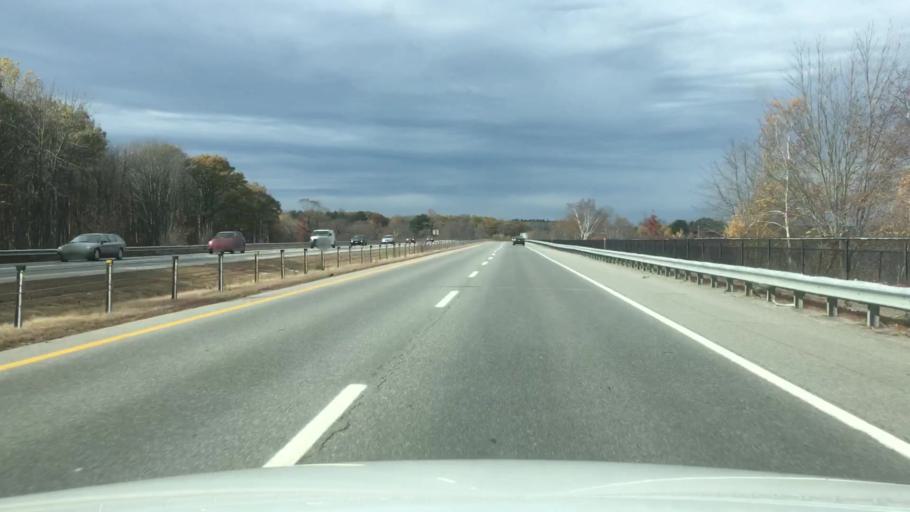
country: US
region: Maine
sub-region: Cumberland County
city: Brunswick
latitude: 43.9102
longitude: -69.9313
